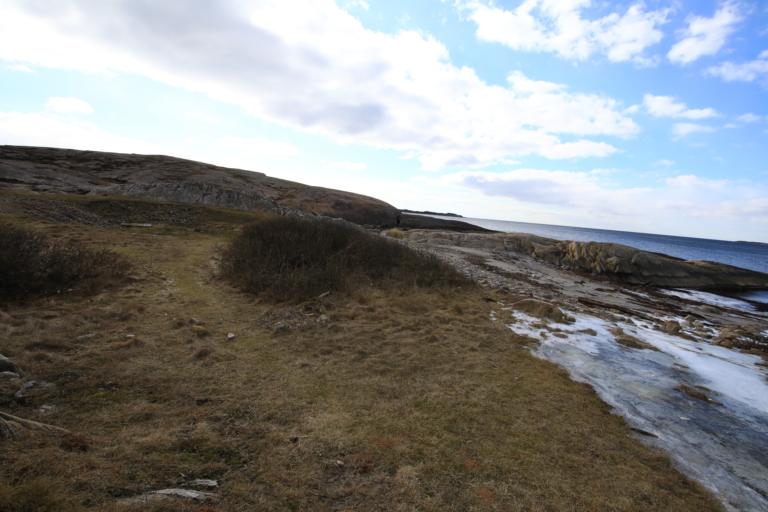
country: SE
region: Halland
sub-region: Kungsbacka Kommun
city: Frillesas
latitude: 57.2183
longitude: 12.1336
